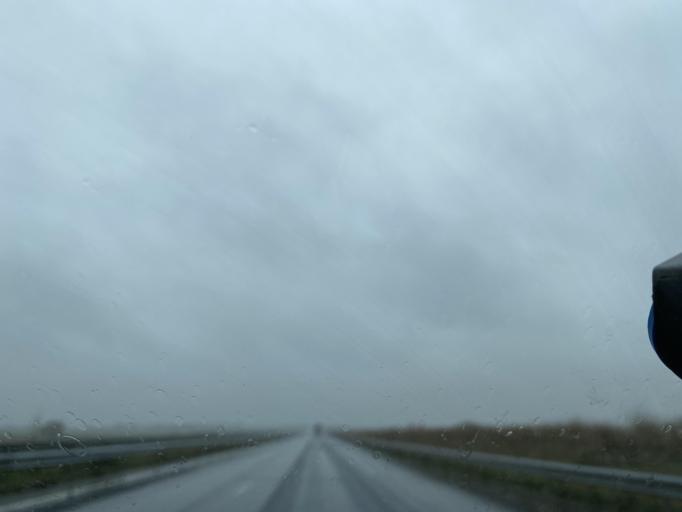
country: FR
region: Centre
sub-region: Departement d'Eure-et-Loir
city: Leves
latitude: 48.5236
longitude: 1.4565
